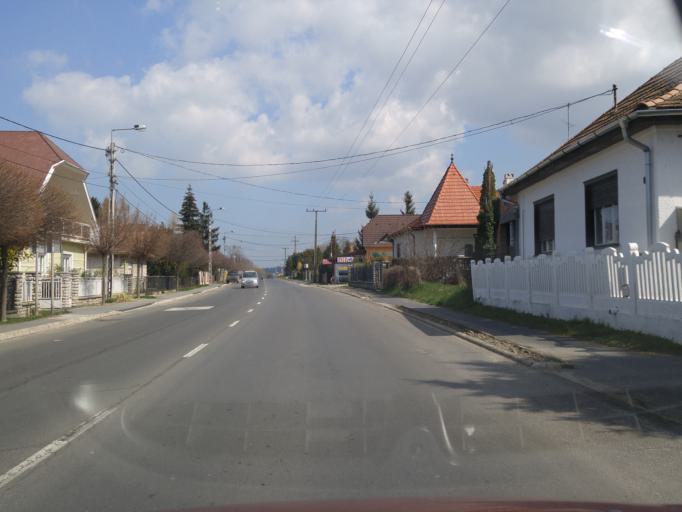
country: HU
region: Somogy
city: Balatonszarszo
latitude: 46.8268
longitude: 17.8377
